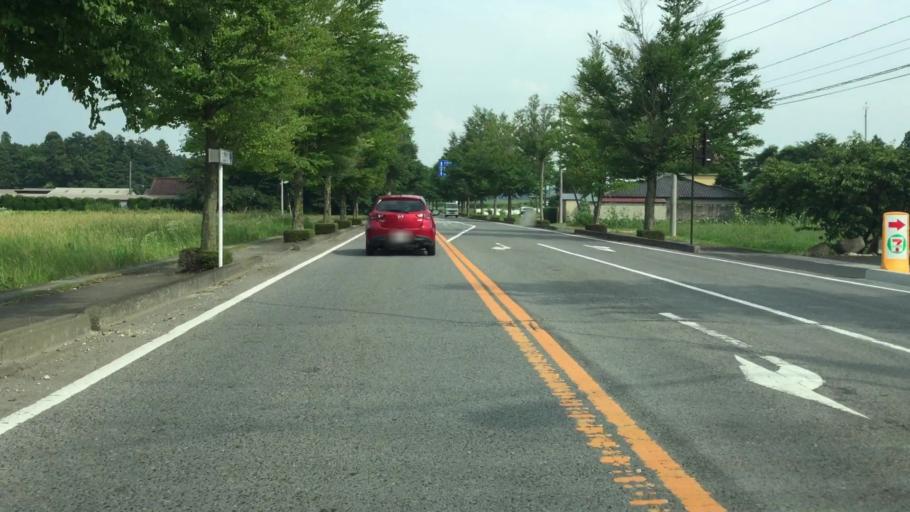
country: JP
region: Tochigi
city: Kuroiso
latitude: 36.9925
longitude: 139.9414
